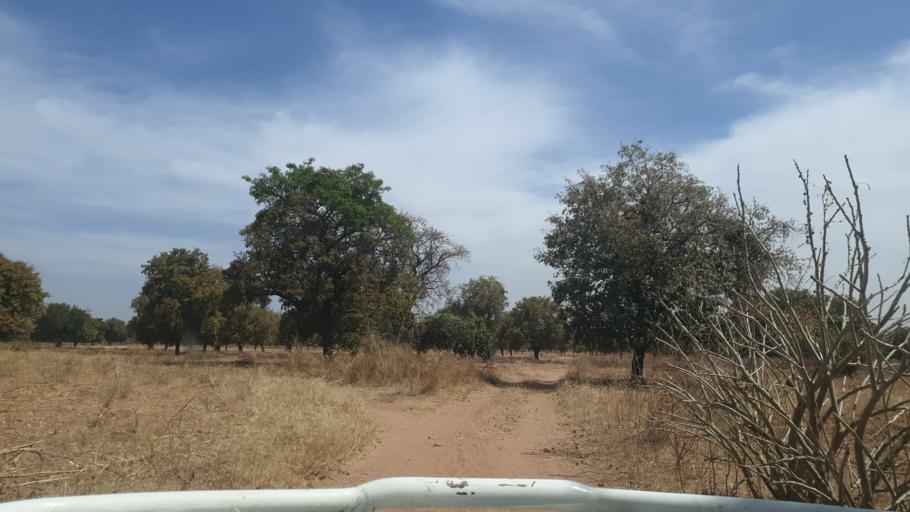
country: ML
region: Sikasso
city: Yorosso
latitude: 12.2874
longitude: -4.6764
